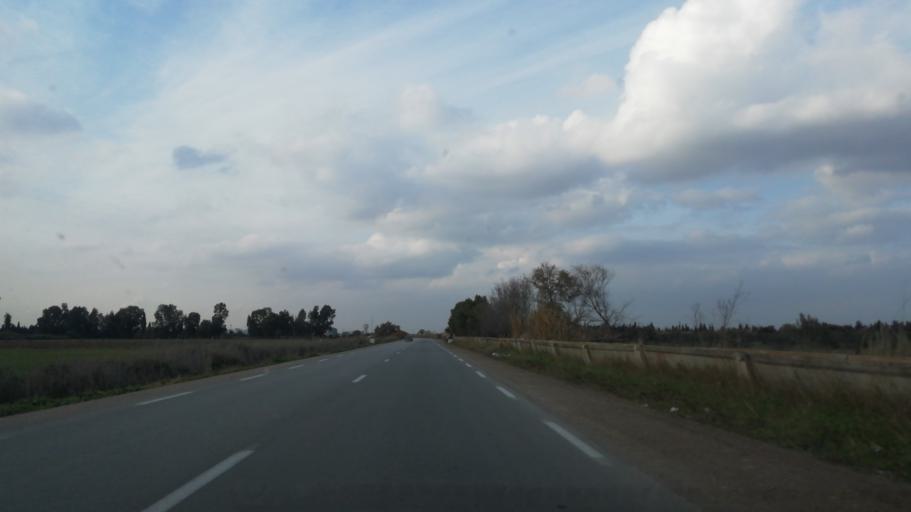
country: DZ
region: Mascara
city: Sig
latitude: 35.6472
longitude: 0.0258
